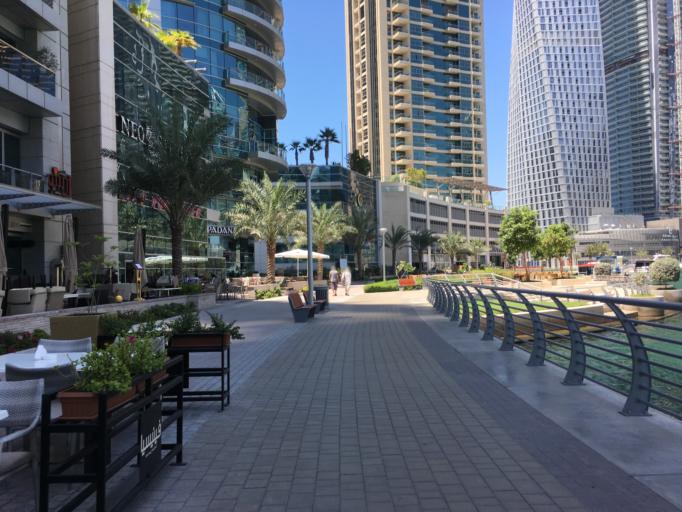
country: AE
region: Dubai
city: Dubai
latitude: 25.0840
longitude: 55.1452
